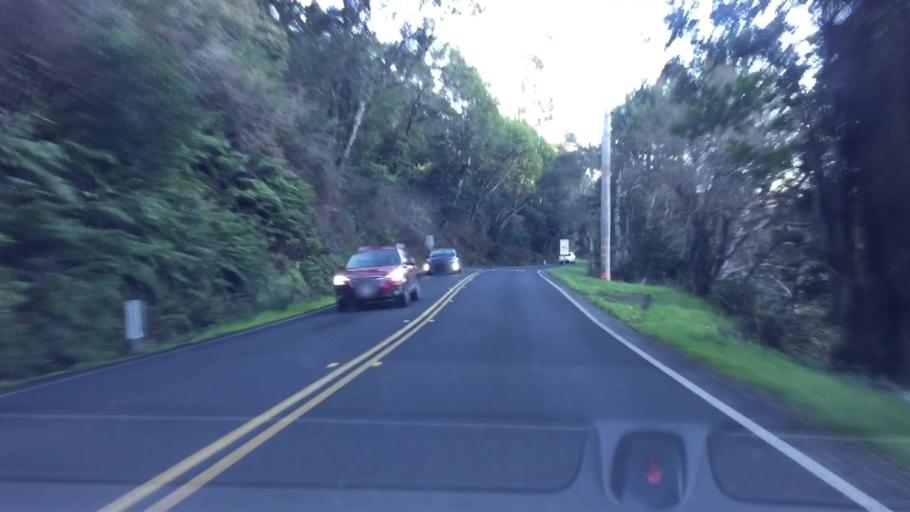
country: US
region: California
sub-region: Marin County
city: Inverness
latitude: 38.0869
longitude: -122.8403
